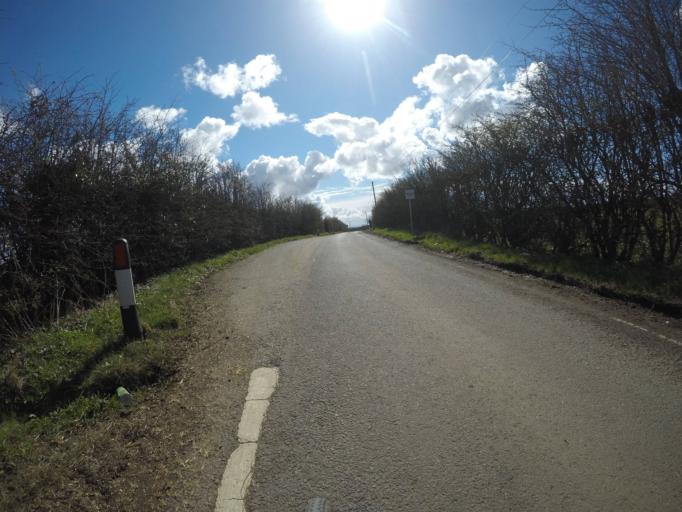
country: GB
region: Scotland
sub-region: North Ayrshire
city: Kilwinning
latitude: 55.6694
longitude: -4.7202
